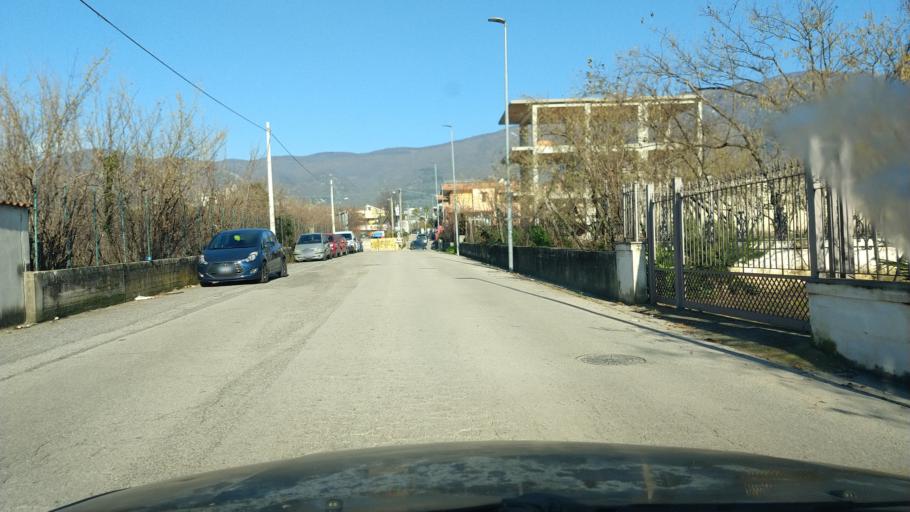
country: IT
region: Campania
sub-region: Provincia di Avellino
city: Sperone
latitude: 40.9516
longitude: 14.5984
